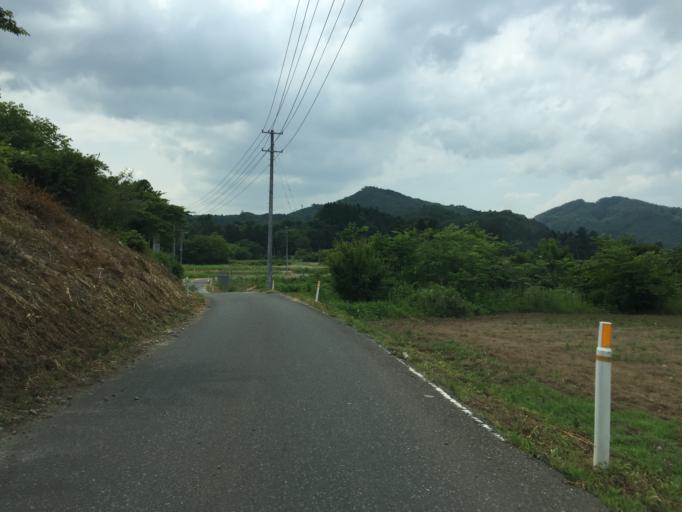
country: JP
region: Miyagi
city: Marumori
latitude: 37.8311
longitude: 140.8375
